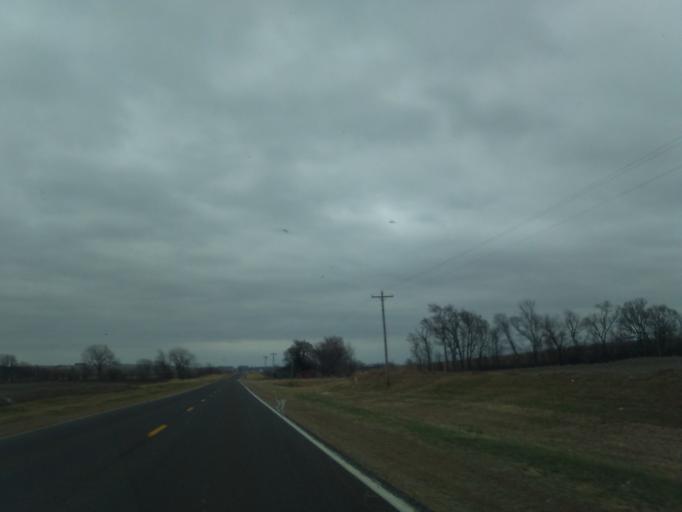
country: US
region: Nebraska
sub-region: Richardson County
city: Falls City
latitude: 40.0581
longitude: -95.5415
